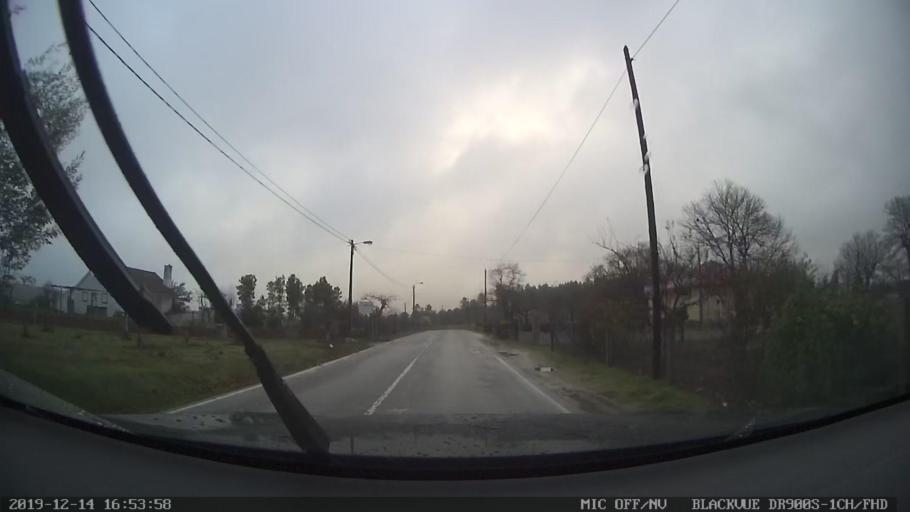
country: PT
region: Vila Real
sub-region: Murca
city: Murca
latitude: 41.4353
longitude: -7.5191
